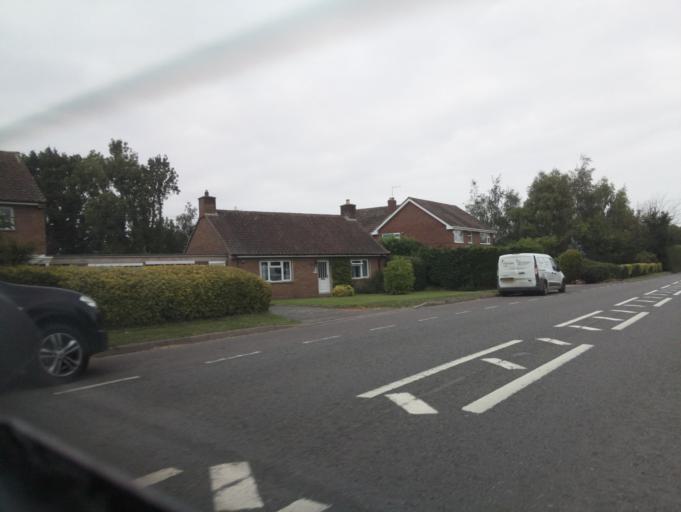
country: GB
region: England
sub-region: Shropshire
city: Shawbury
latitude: 52.7888
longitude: -2.6471
